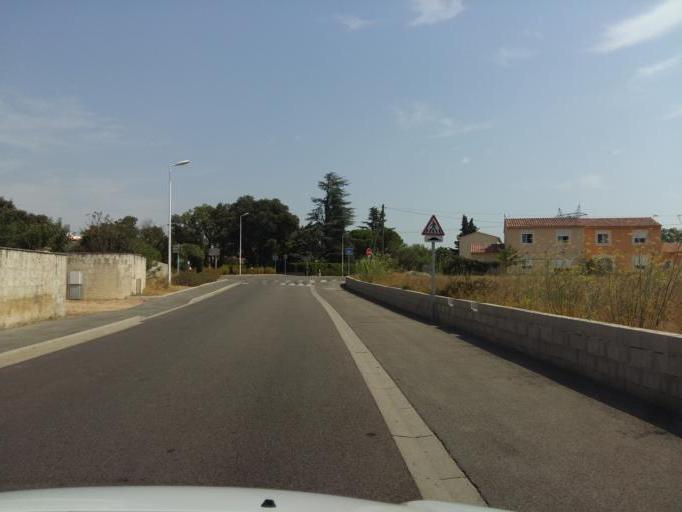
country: FR
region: Provence-Alpes-Cote d'Azur
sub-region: Departement du Vaucluse
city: Bollene
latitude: 44.2903
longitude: 4.7577
